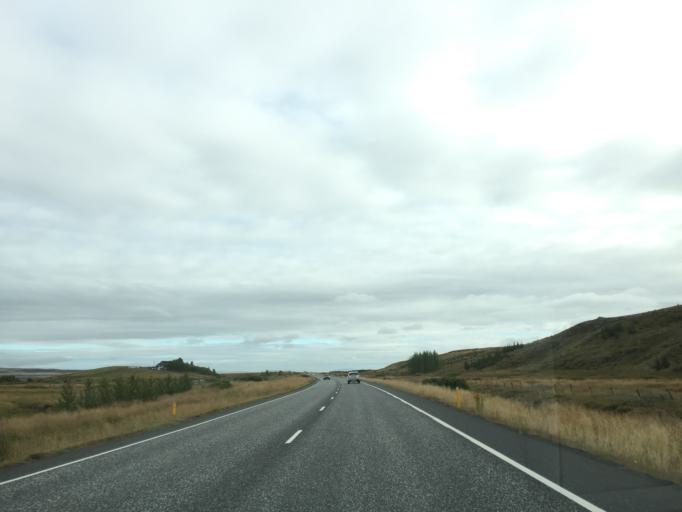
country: IS
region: South
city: Selfoss
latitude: 63.9483
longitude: -20.7410
